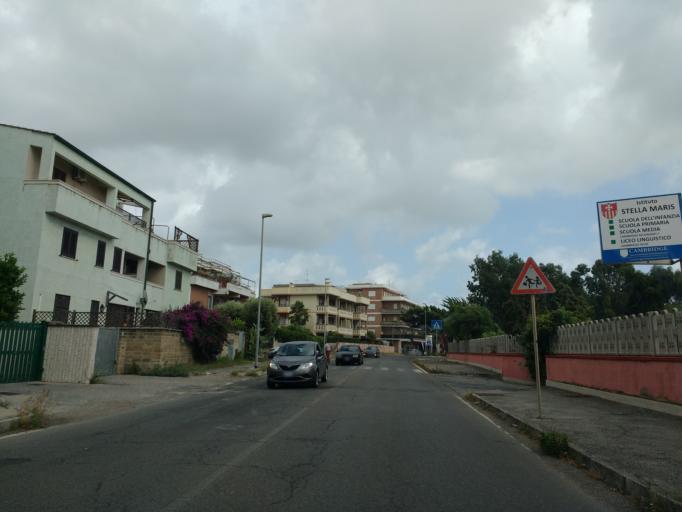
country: IT
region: Latium
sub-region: Citta metropolitana di Roma Capitale
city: Anzio
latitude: 41.4684
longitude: 12.6090
